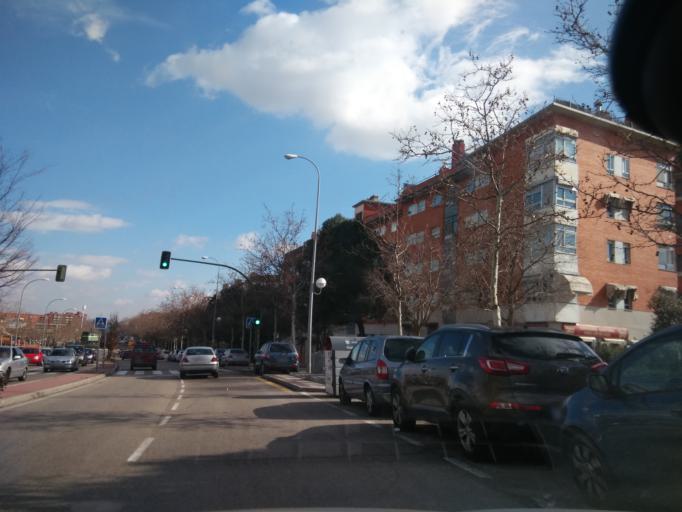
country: ES
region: Madrid
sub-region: Provincia de Madrid
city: Alcobendas
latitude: 40.5477
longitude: -3.6595
